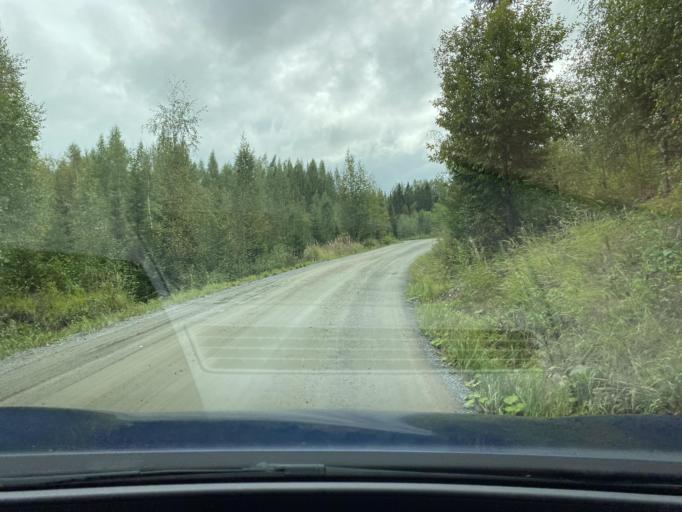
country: FI
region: Pirkanmaa
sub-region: Lounais-Pirkanmaa
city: Vammala
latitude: 61.2581
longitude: 23.0148
